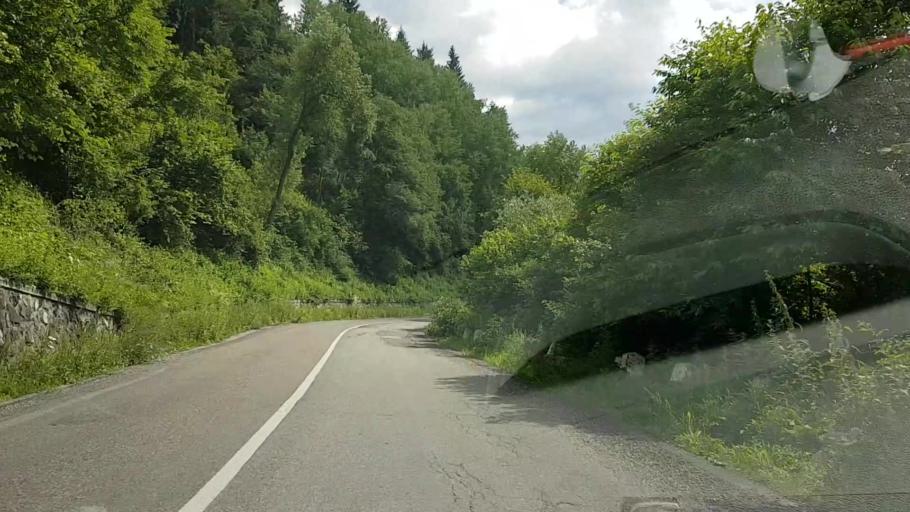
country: RO
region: Neamt
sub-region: Comuna Ceahlau
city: Ceahlau
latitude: 47.0747
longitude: 25.9637
